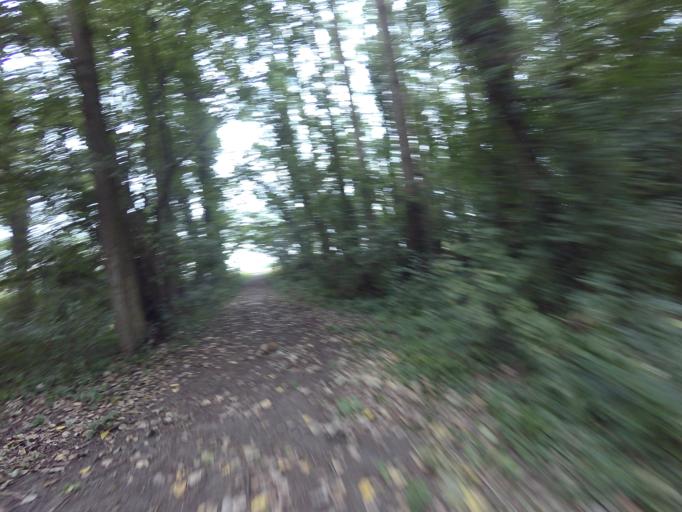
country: BE
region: Flanders
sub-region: Provincie Vlaams-Brabant
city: Kampenhout
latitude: 50.9506
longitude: 4.5376
